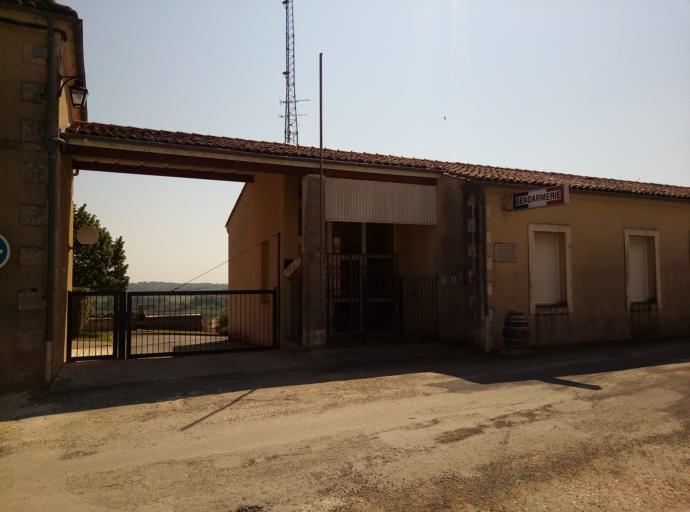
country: FR
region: Poitou-Charentes
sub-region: Departement de la Charente
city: Chalais
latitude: 45.3306
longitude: -0.0441
